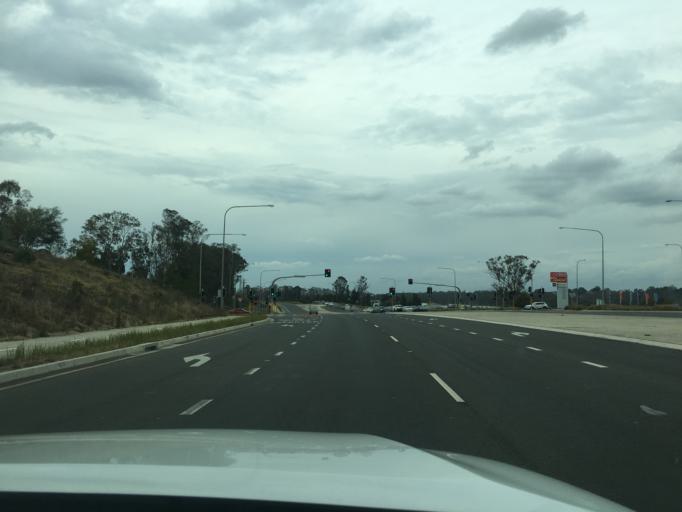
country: AU
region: New South Wales
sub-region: Campbelltown Municipality
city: Denham Court
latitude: -33.9768
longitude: 150.8086
